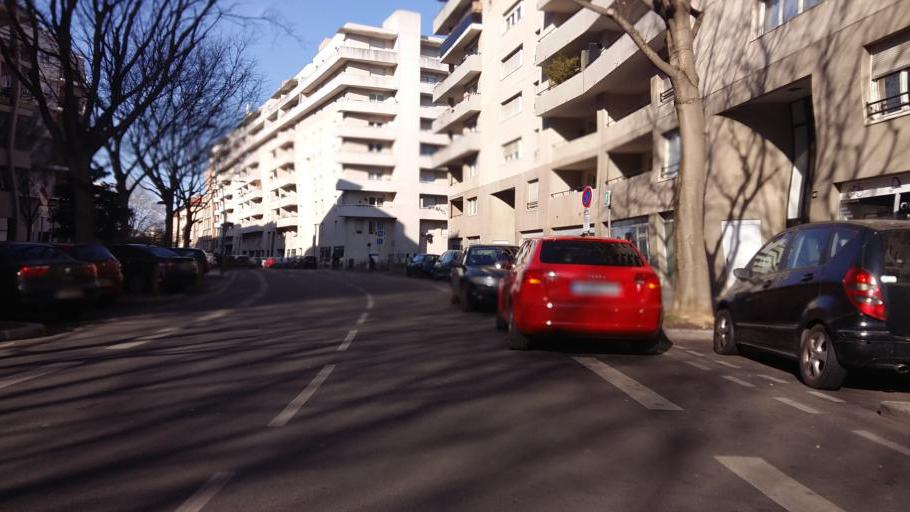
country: FR
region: Rhone-Alpes
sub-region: Departement du Rhone
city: Villeurbanne
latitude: 45.7725
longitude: 4.8739
